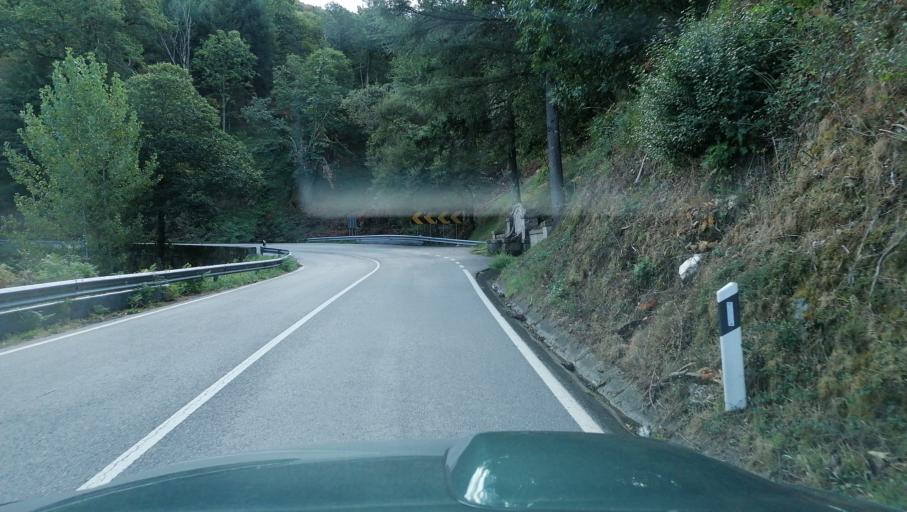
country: PT
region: Vila Real
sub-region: Vila Pouca de Aguiar
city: Vila Pouca de Aguiar
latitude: 41.5065
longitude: -7.6245
